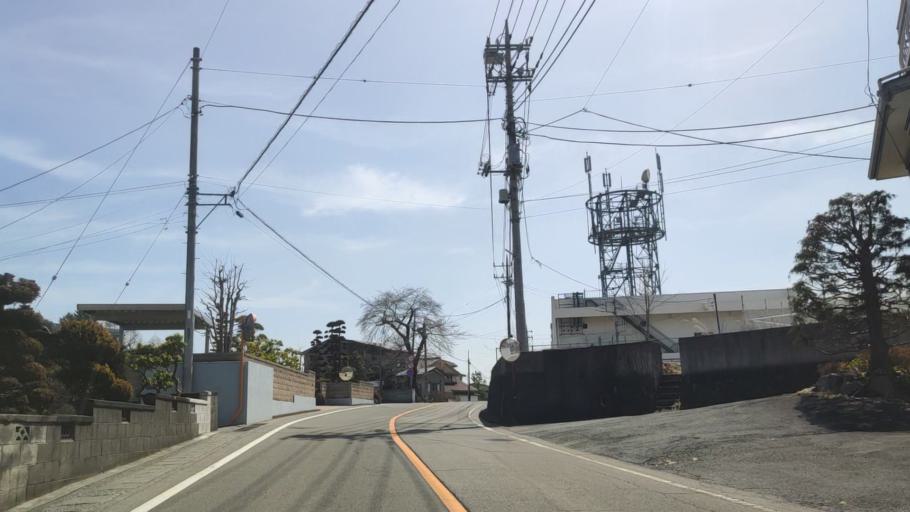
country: JP
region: Yamanashi
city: Fujikawaguchiko
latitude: 35.5010
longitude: 138.7609
